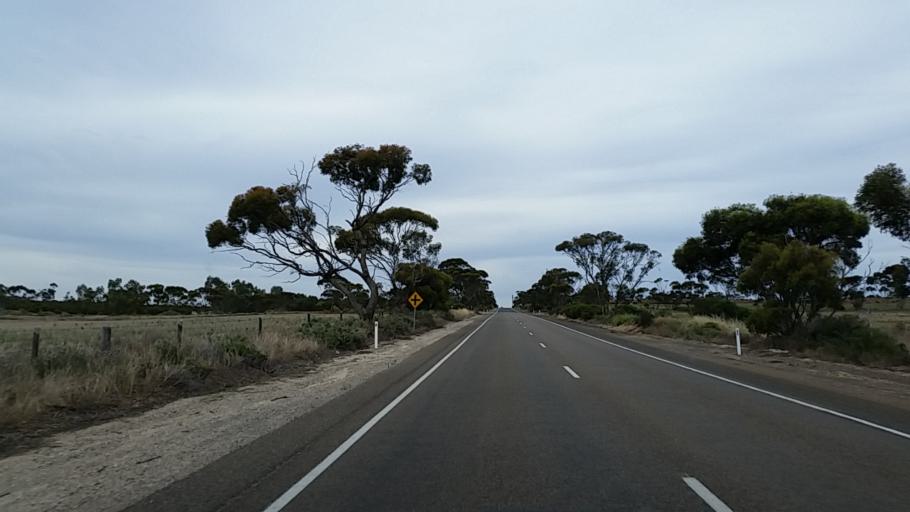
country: AU
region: South Australia
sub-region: Mid Murray
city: Mannum
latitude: -34.9225
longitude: 139.2553
